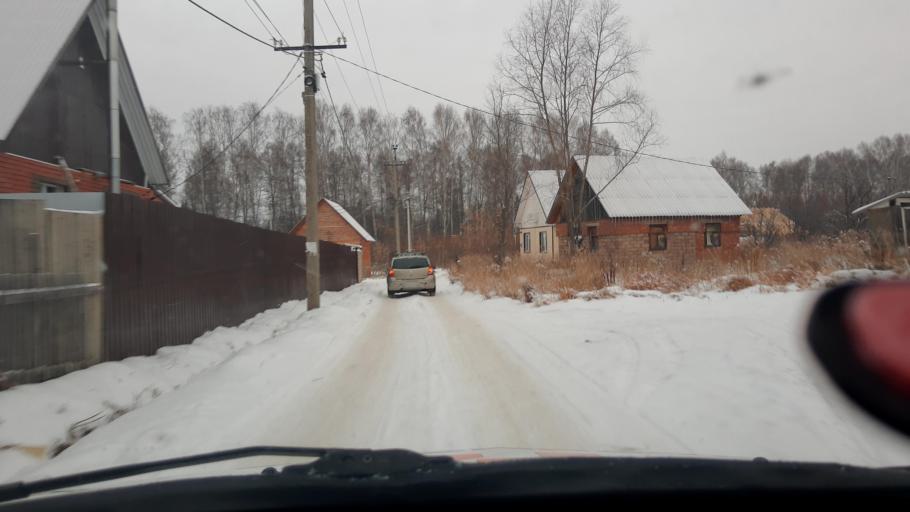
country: RU
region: Bashkortostan
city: Iglino
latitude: 54.8427
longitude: 56.4649
